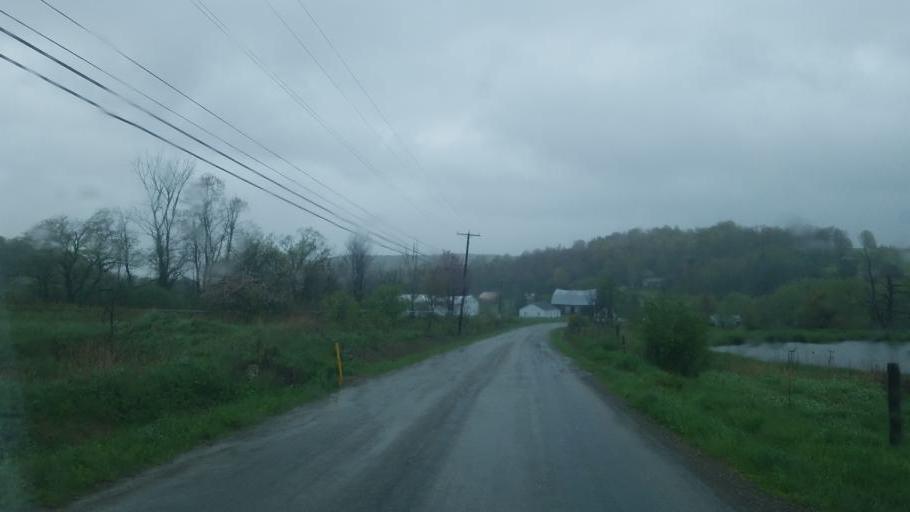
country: US
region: Pennsylvania
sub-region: Potter County
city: Galeton
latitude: 41.9185
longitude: -77.7785
